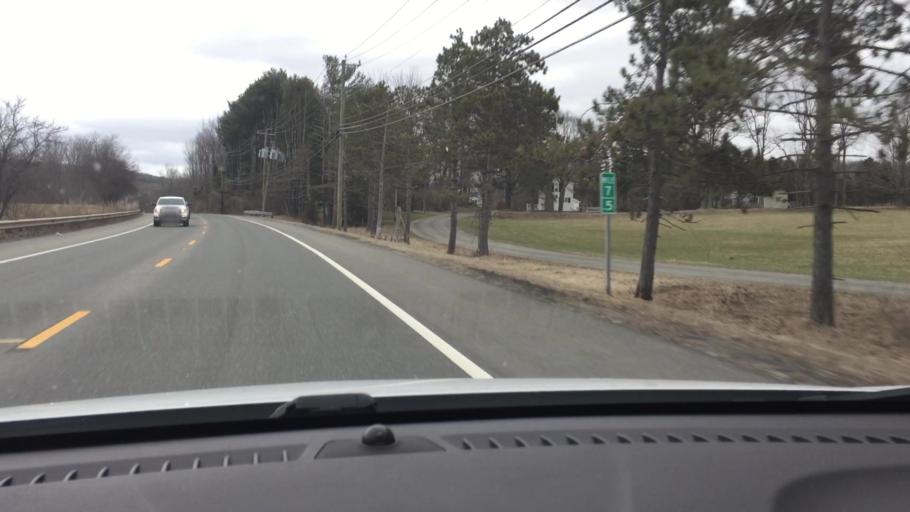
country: US
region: Massachusetts
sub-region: Berkshire County
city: Dalton
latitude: 42.4855
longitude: -73.1361
